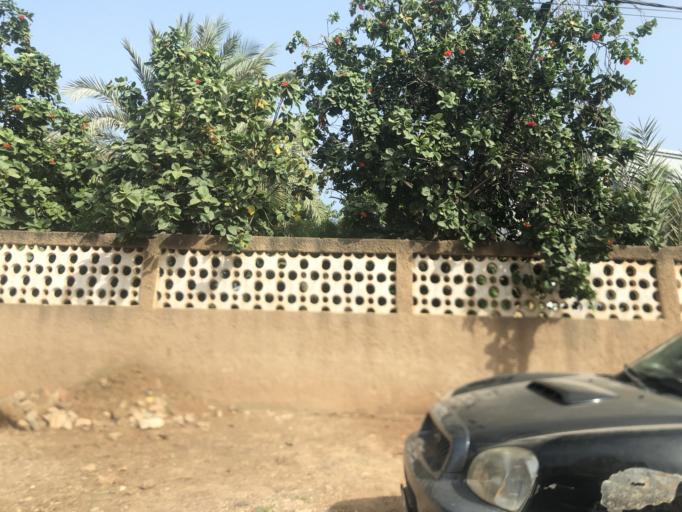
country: SN
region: Dakar
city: Mermoz Boabab
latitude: 14.7311
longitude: -17.4987
